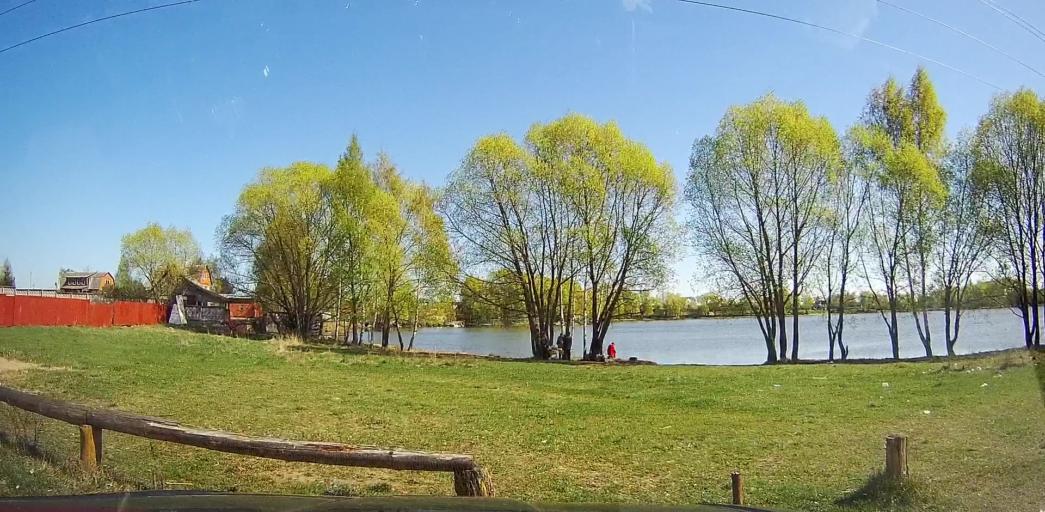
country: RU
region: Moskovskaya
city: Bronnitsy
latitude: 55.4740
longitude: 38.2534
